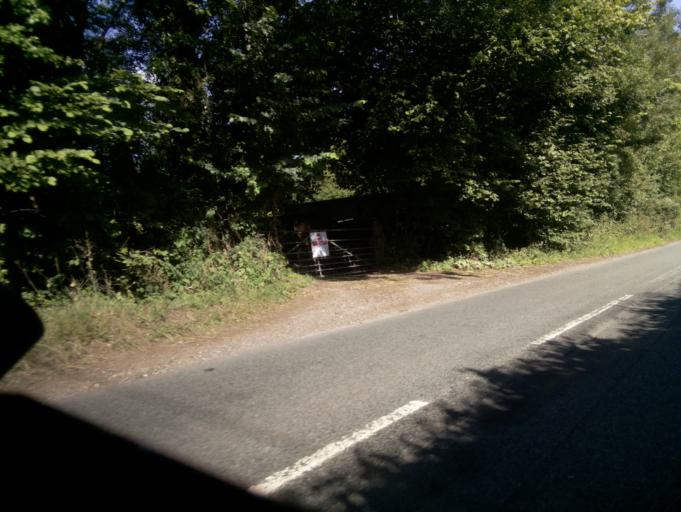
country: GB
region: England
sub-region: Herefordshire
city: Yatton
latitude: 51.9421
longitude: -2.5264
